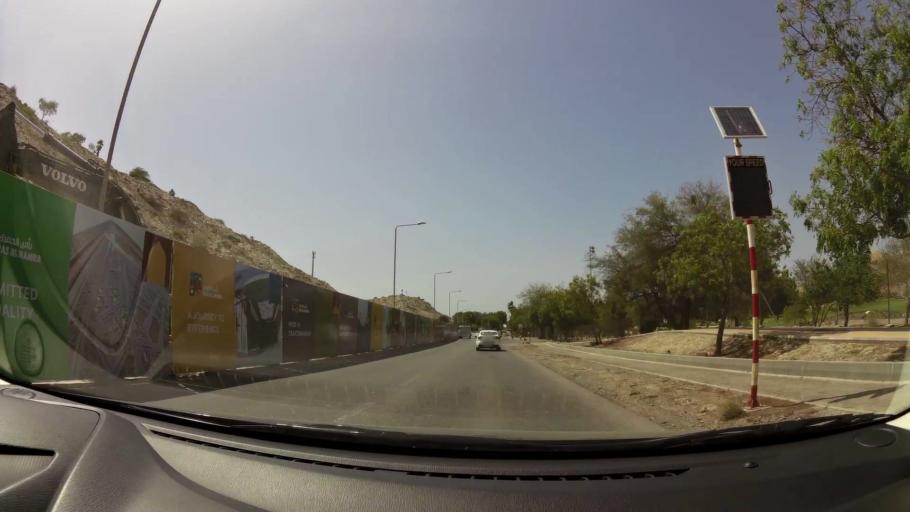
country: OM
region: Muhafazat Masqat
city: Muscat
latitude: 23.6371
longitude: 58.4987
